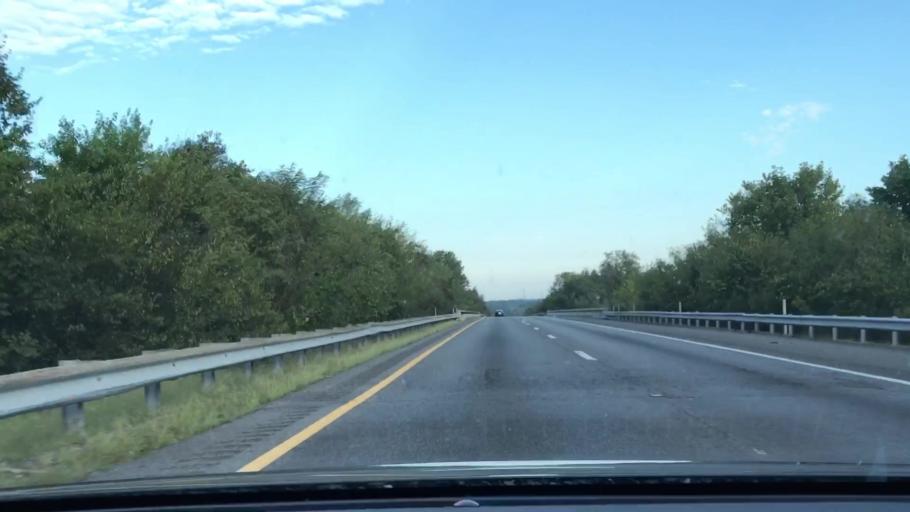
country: US
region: Kentucky
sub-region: Todd County
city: Guthrie
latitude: 36.5248
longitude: -87.2200
